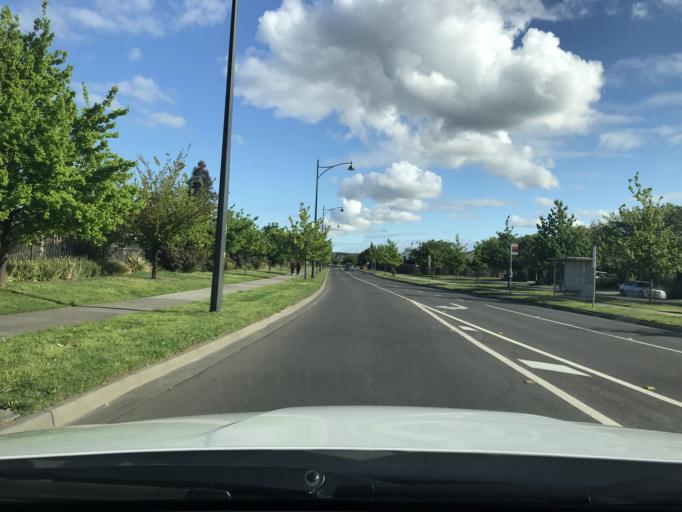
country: AU
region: Victoria
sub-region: Hume
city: Roxburgh Park
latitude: -37.5852
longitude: 144.9066
